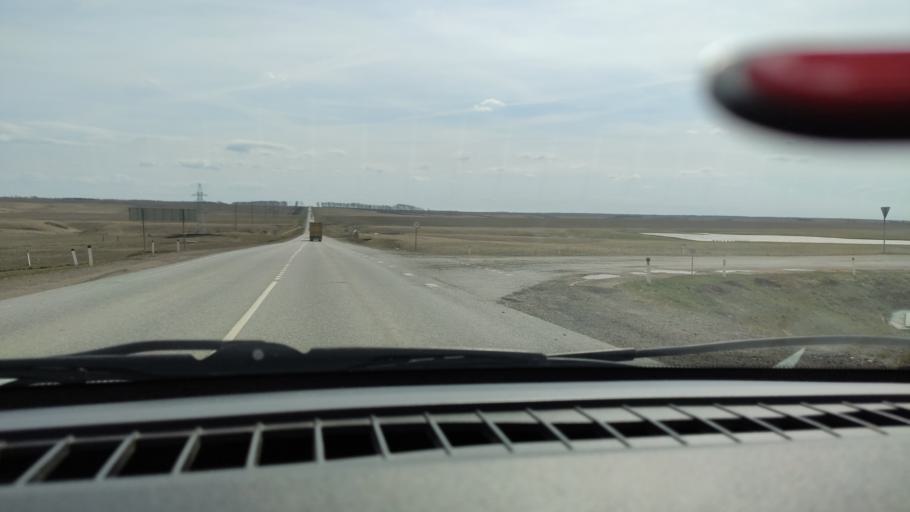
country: RU
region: Bashkortostan
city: Dyurtyuli
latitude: 55.3264
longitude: 54.9689
